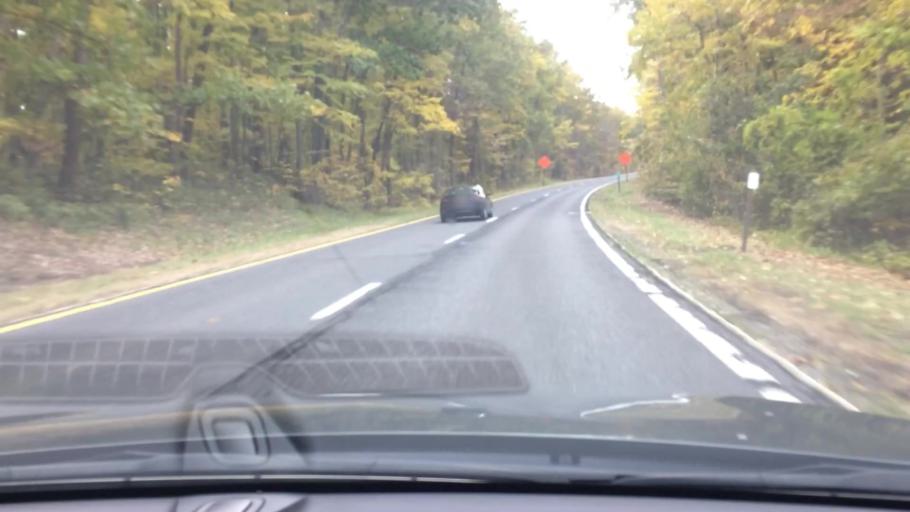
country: US
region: New York
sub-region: Dutchess County
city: Pleasant Valley
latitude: 41.6970
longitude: -73.7831
